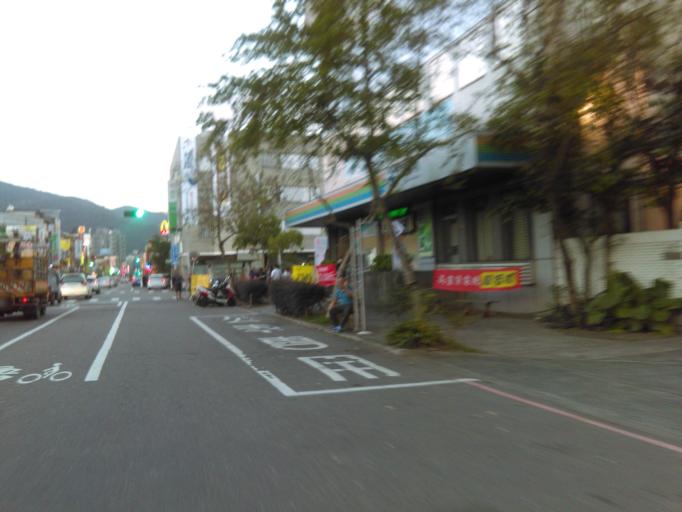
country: TW
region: Taiwan
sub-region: Yilan
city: Yilan
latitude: 24.8210
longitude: 121.7696
